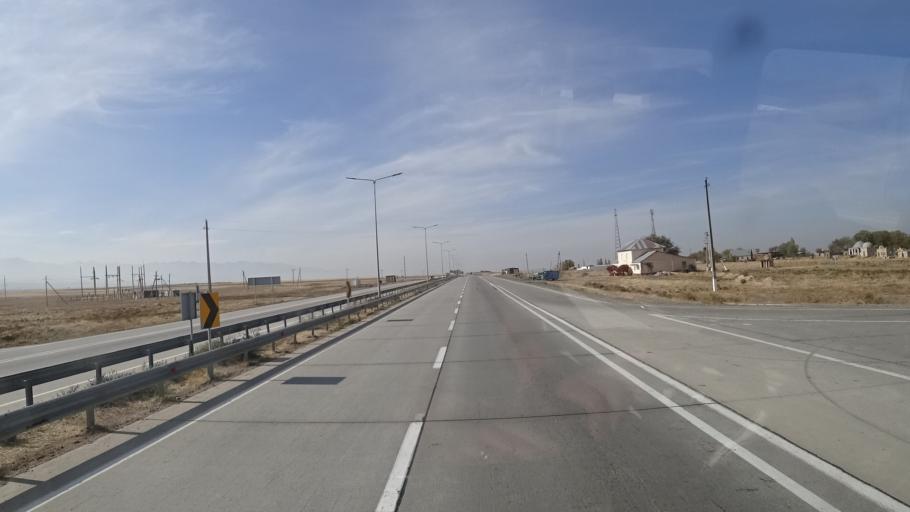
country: KZ
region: Zhambyl
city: Merke
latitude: 42.8892
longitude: 72.9879
